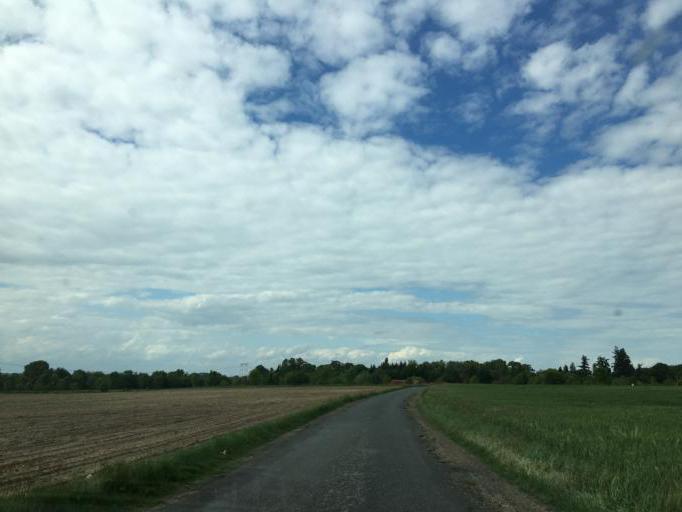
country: FR
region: Centre
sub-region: Departement du Loiret
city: Dry
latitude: 47.7819
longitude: 1.7012
